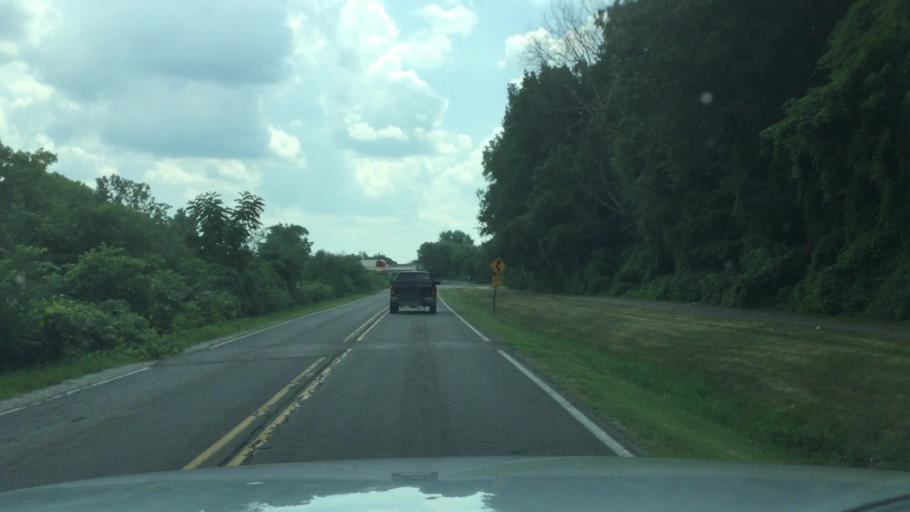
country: US
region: Michigan
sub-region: Washtenaw County
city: Ypsilanti
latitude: 42.2239
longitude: -83.5629
